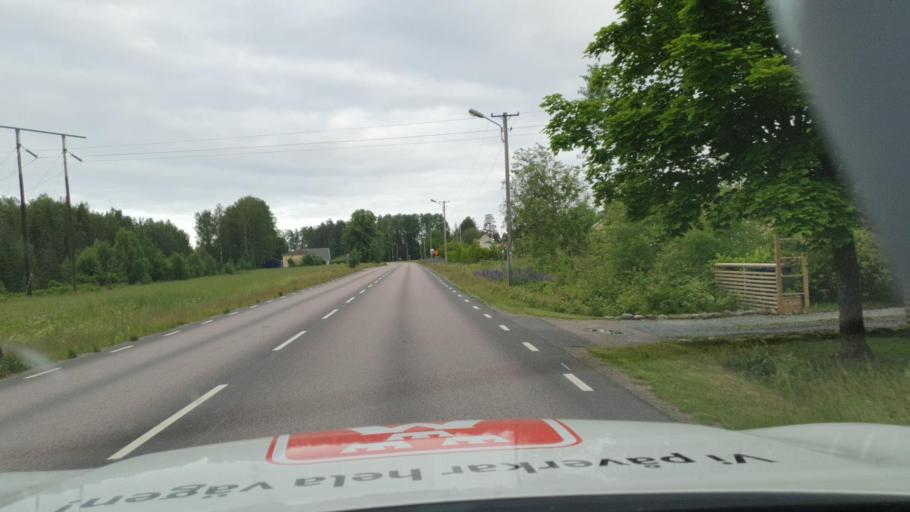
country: SE
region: Vaermland
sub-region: Forshaga Kommun
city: Forshaga
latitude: 59.4545
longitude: 13.4224
